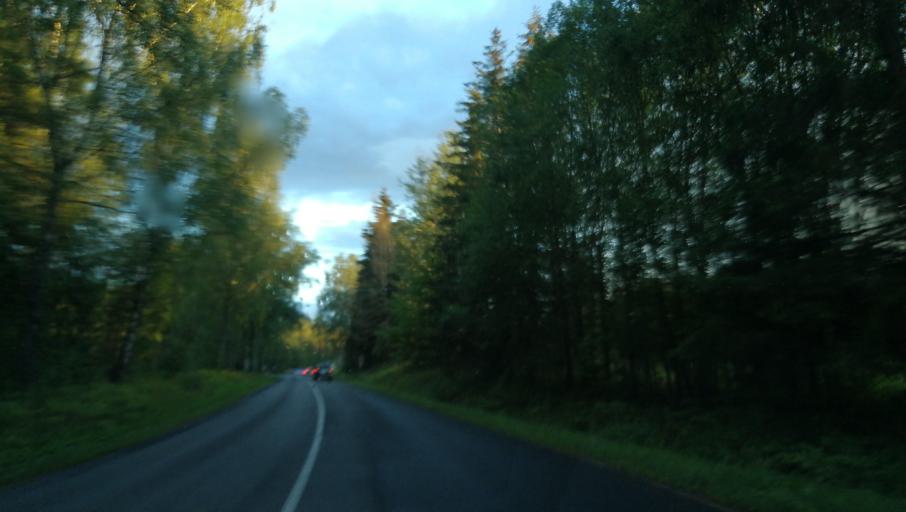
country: LV
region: Priekuli
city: Priekuli
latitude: 57.3672
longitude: 25.3814
